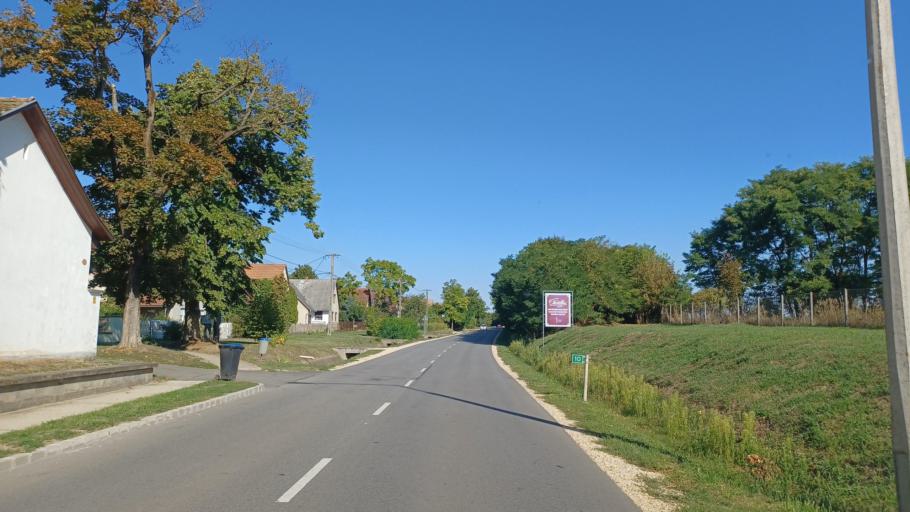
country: HU
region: Tolna
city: Nemetker
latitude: 46.6822
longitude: 18.8055
